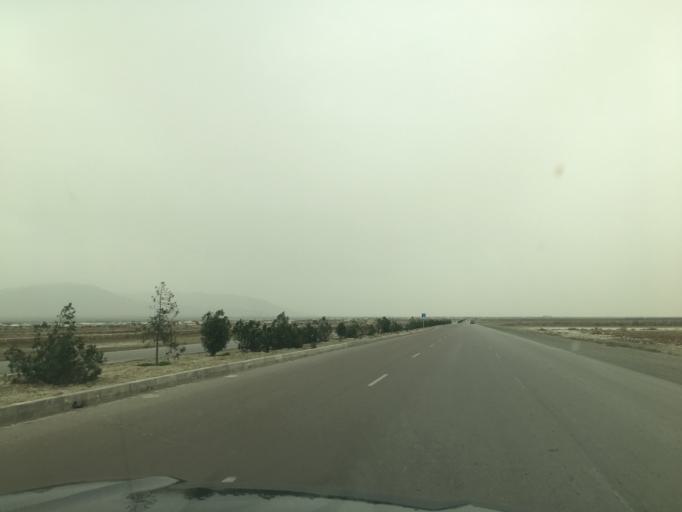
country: TM
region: Ahal
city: Baharly
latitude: 38.3741
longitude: 57.5121
